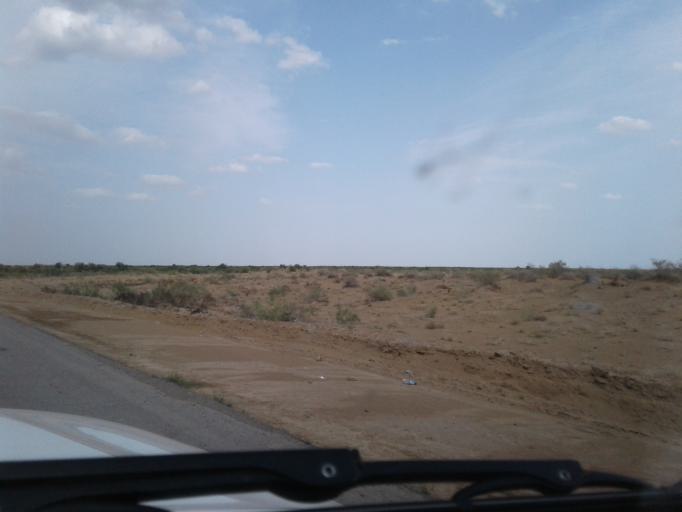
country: TM
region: Mary
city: Mary
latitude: 37.2837
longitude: 61.3266
